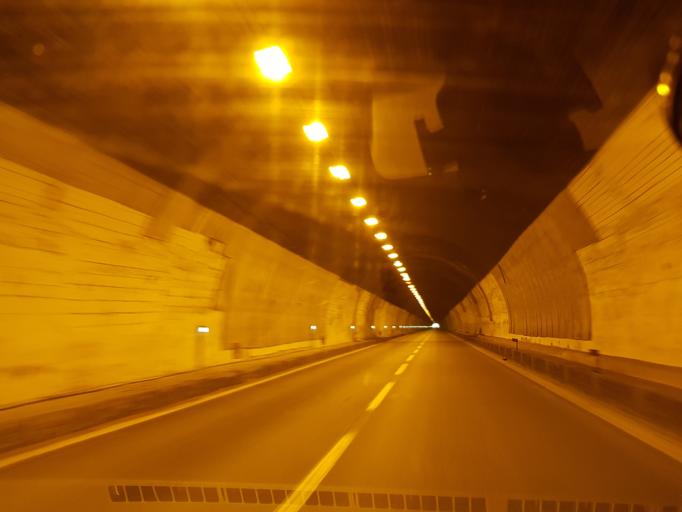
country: IT
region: Liguria
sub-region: Provincia di Genova
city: Ronco Scrivia
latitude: 44.6154
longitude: 8.9559
